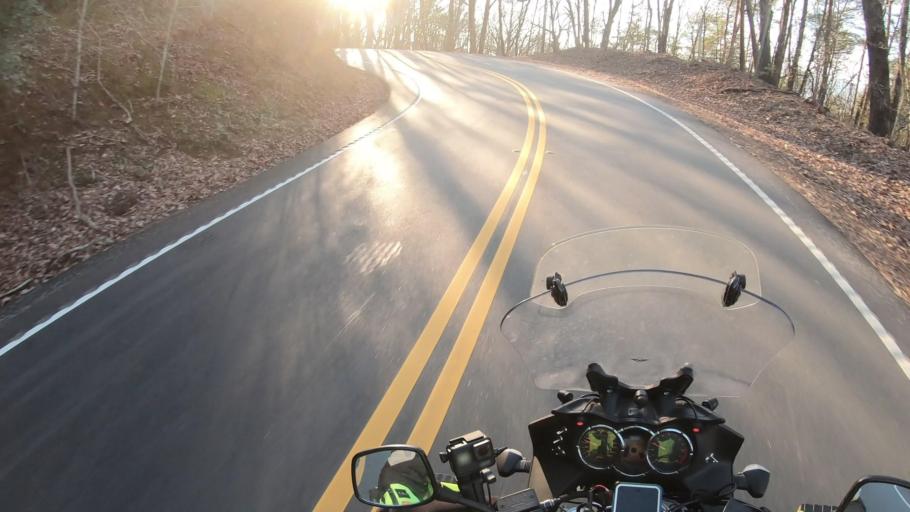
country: US
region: Georgia
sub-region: Lumpkin County
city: Dahlonega
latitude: 34.6243
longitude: -83.9563
